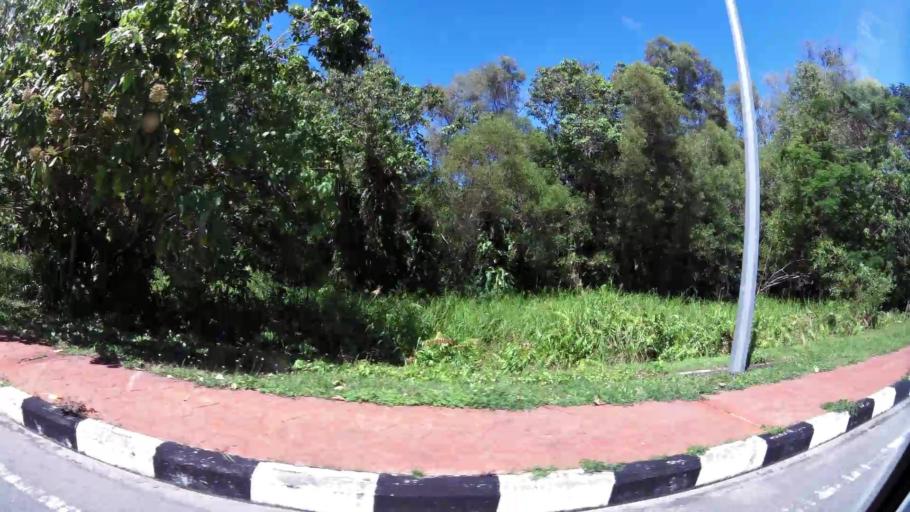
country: BN
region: Brunei and Muara
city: Bandar Seri Begawan
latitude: 5.0308
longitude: 115.0702
